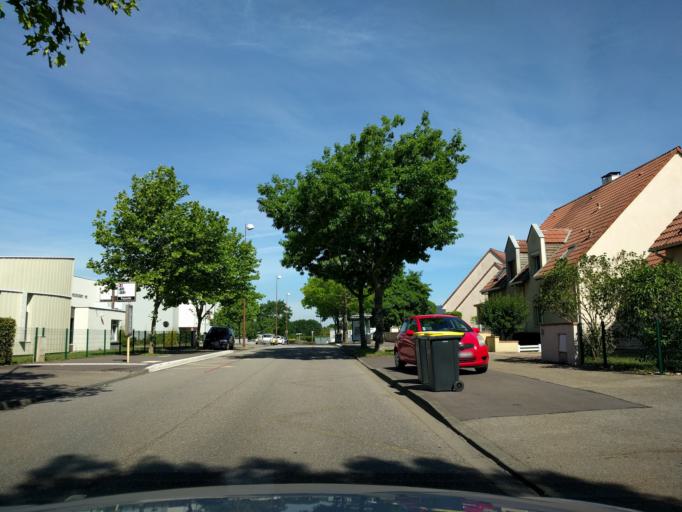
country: FR
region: Lorraine
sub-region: Departement de la Moselle
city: Peltre
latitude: 49.0927
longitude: 6.2402
